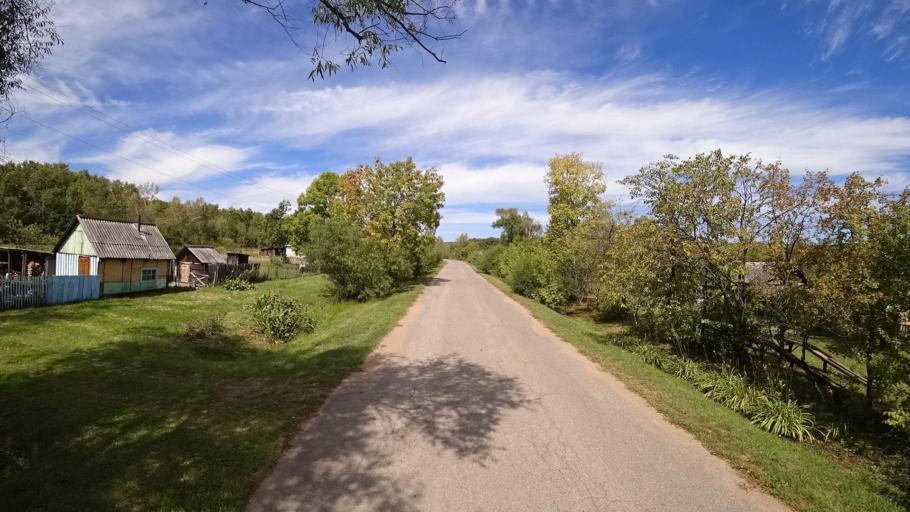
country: RU
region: Primorskiy
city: Yakovlevka
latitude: 44.6503
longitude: 133.5974
